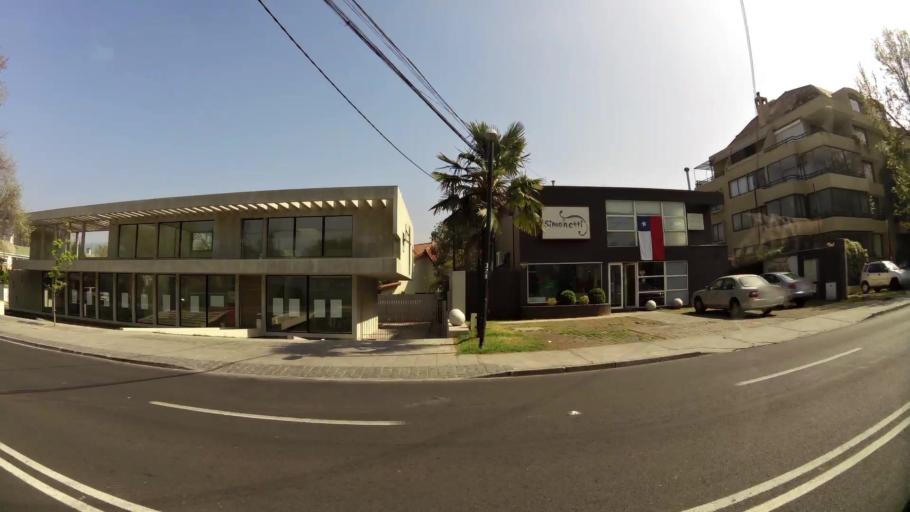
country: CL
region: Santiago Metropolitan
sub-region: Provincia de Santiago
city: Villa Presidente Frei, Nunoa, Santiago, Chile
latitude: -33.3852
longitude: -70.5747
